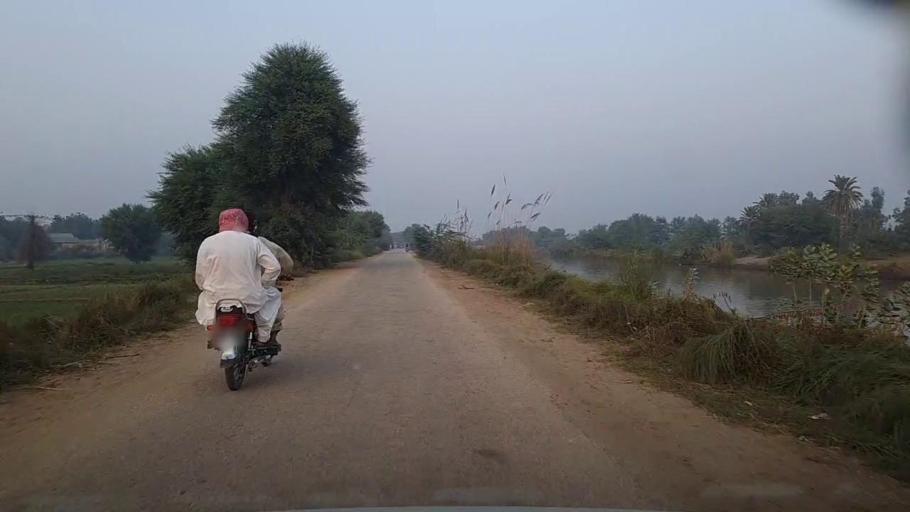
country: PK
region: Sindh
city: Bozdar
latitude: 27.0477
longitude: 68.5946
